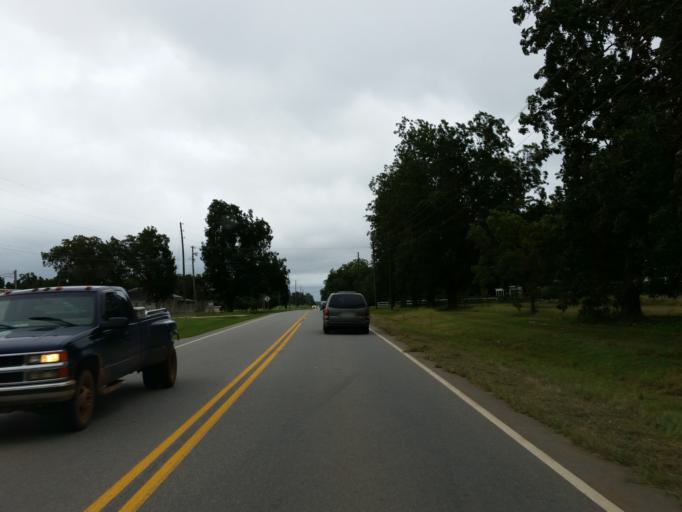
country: US
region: Georgia
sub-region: Peach County
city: Fort Valley
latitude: 32.5871
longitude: -83.9291
